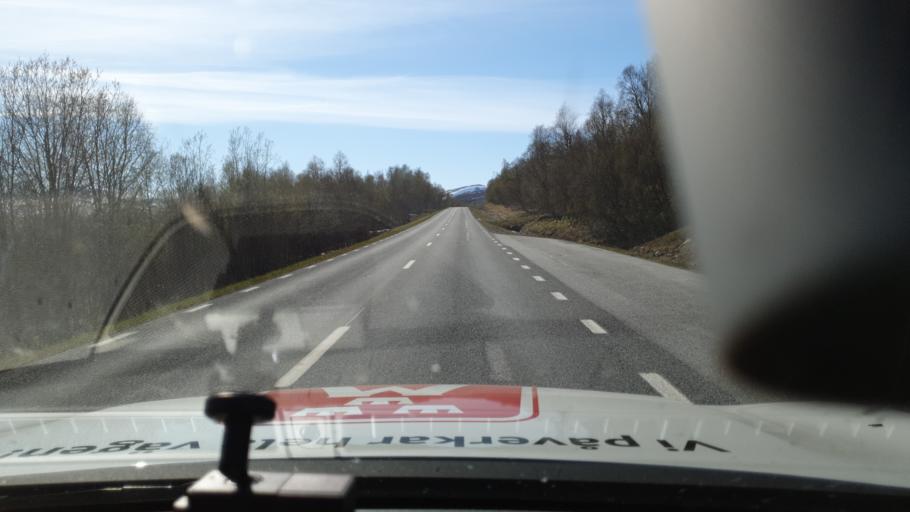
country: NO
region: Nordland
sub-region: Rana
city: Mo i Rana
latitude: 66.0482
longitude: 14.9598
